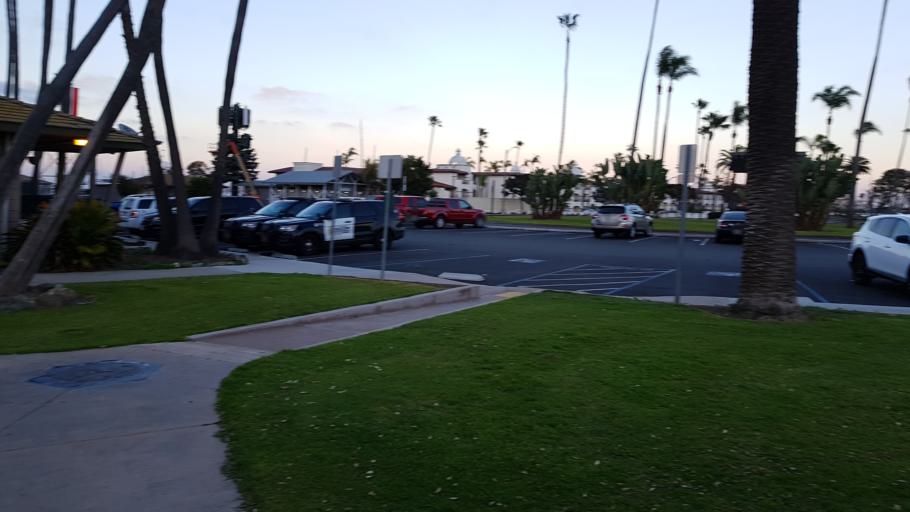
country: US
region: California
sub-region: San Diego County
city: Coronado
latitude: 32.7083
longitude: -117.2346
